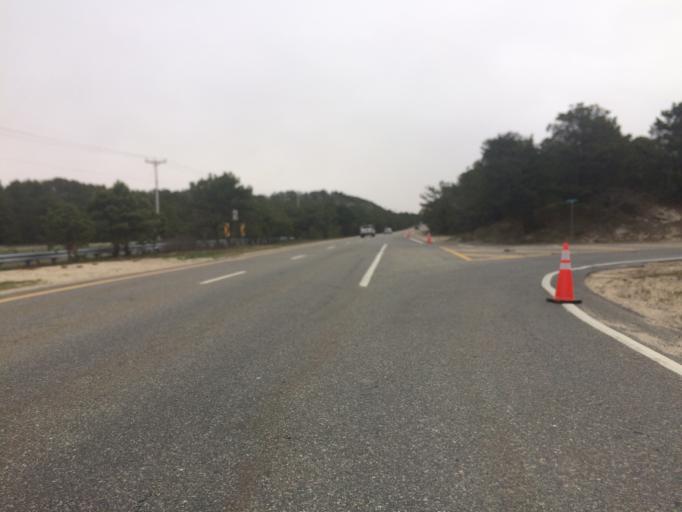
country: US
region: Massachusetts
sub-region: Barnstable County
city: Provincetown
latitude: 42.0622
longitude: -70.1817
